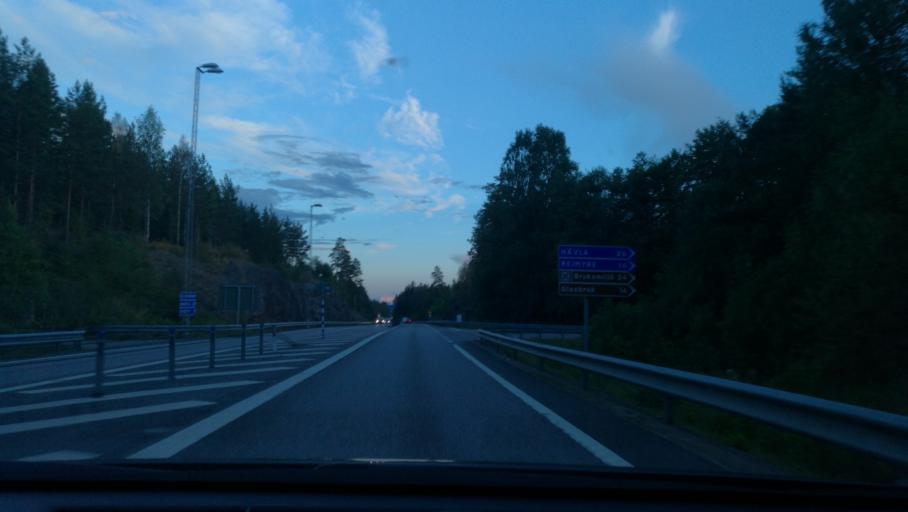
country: SE
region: OEstergoetland
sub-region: Norrkopings Kommun
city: Jursla
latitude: 58.7972
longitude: 16.1549
